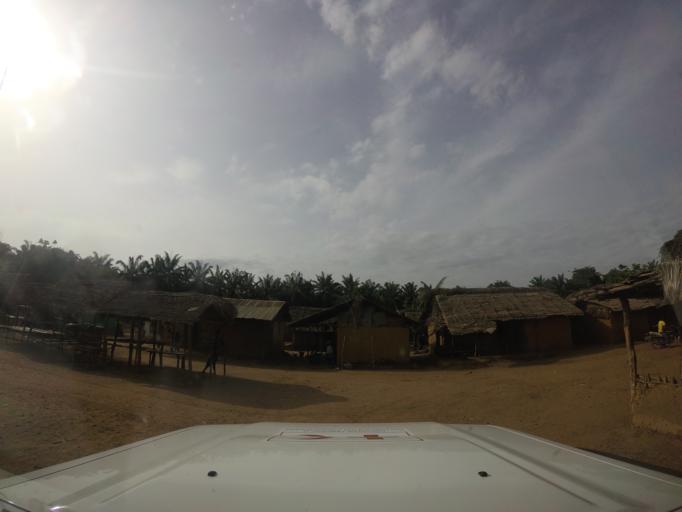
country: LR
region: Grand Cape Mount
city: Robertsport
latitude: 6.8957
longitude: -11.3353
